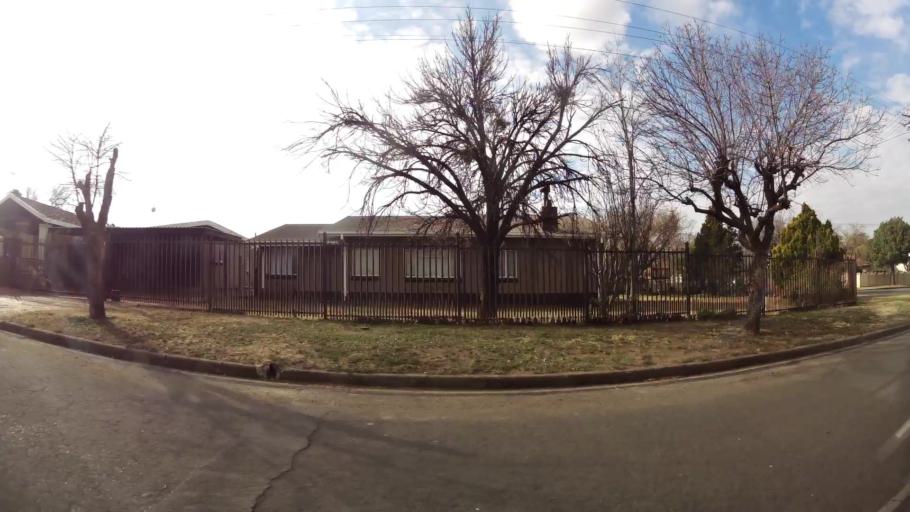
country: ZA
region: Orange Free State
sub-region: Mangaung Metropolitan Municipality
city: Bloemfontein
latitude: -29.0827
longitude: 26.2102
